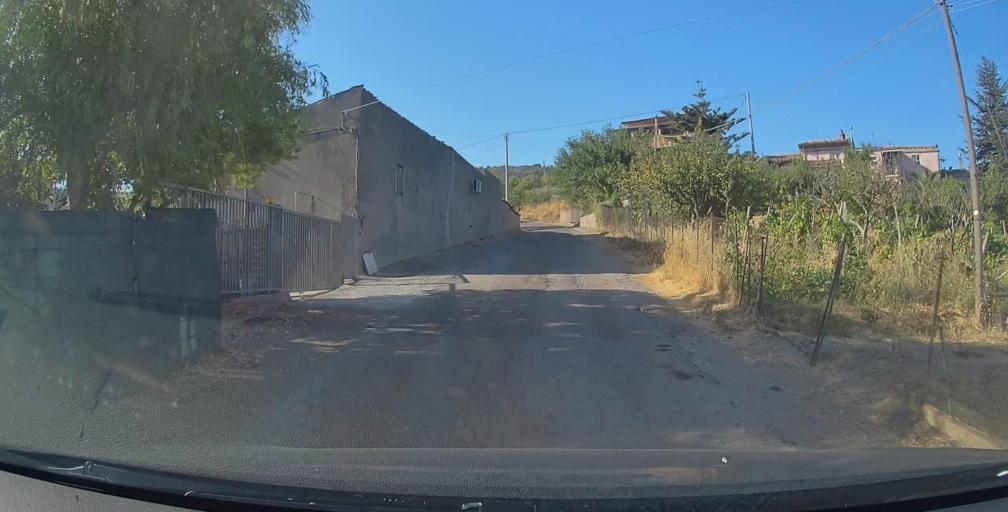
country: IT
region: Sicily
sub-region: Messina
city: San Piero Patti
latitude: 38.0631
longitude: 14.9892
